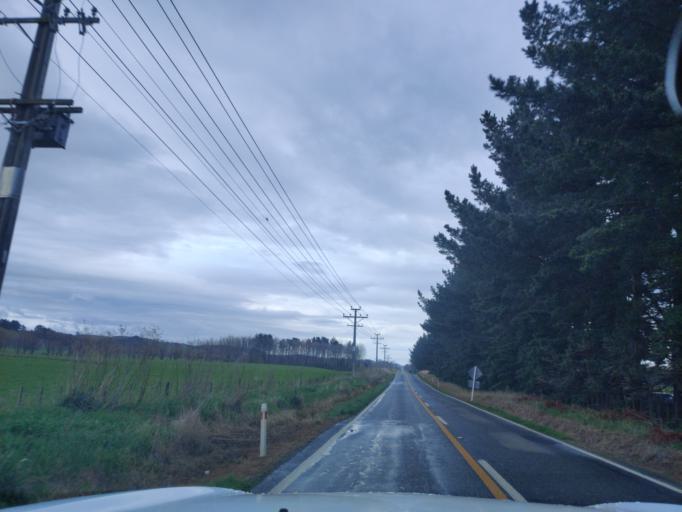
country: NZ
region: Manawatu-Wanganui
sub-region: Palmerston North City
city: Palmerston North
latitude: -40.3365
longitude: 175.7262
